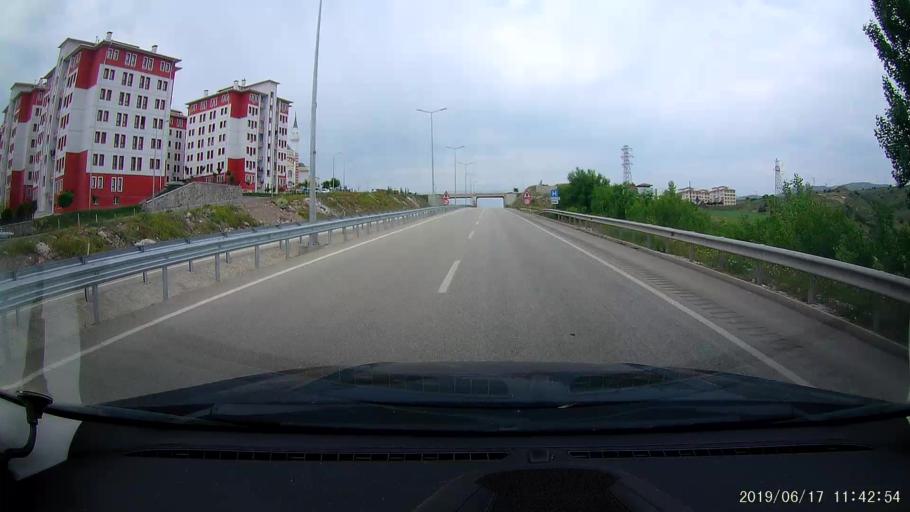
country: TR
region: Cankiri
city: Kursunlu
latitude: 40.8386
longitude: 33.2900
